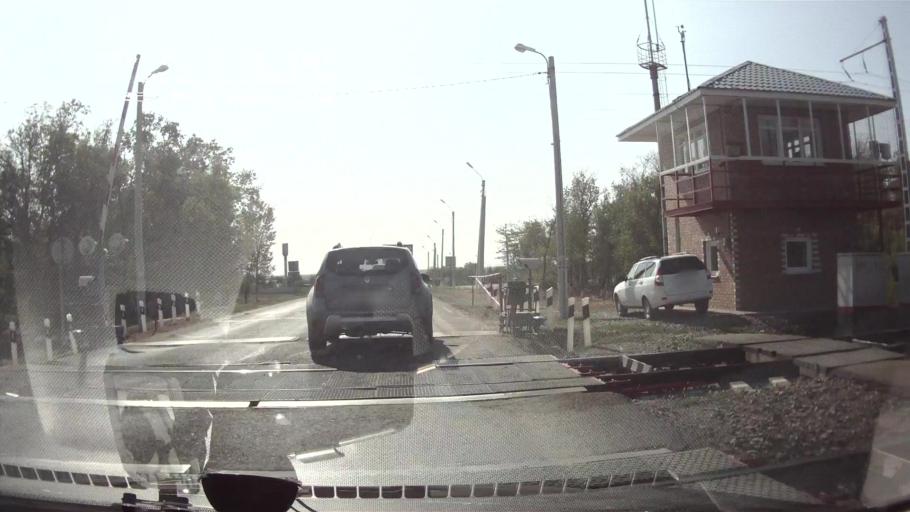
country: RU
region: Krasnodarskiy
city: Belaya Glina
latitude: 46.1000
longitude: 40.8538
